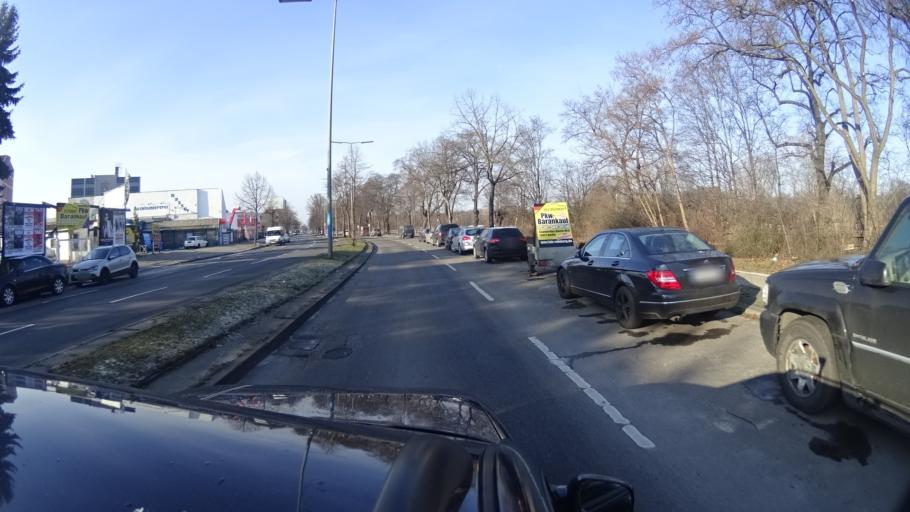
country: DE
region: Berlin
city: Reinickendorf
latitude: 52.5475
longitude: 13.3165
